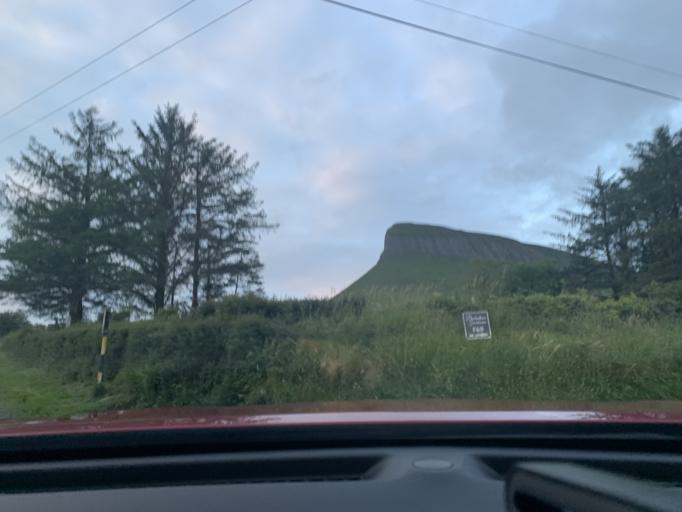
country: IE
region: Connaught
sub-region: Sligo
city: Sligo
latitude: 54.3581
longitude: -8.5045
